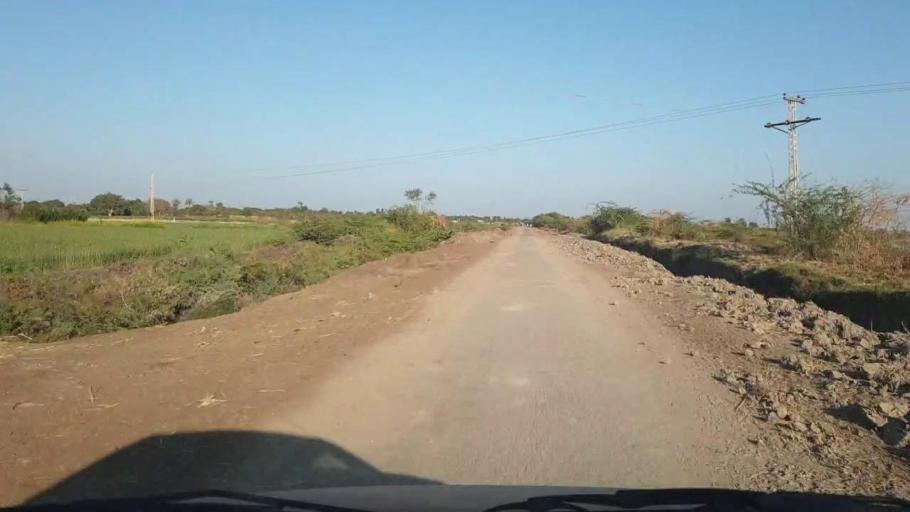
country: PK
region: Sindh
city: Samaro
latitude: 25.3269
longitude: 69.3168
